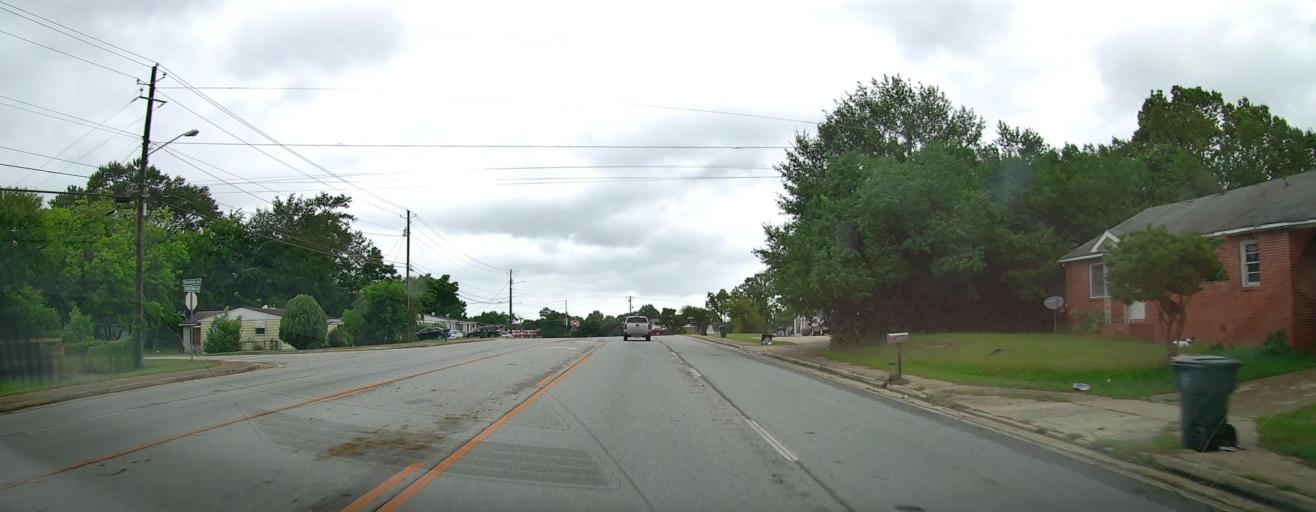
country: US
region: Georgia
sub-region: Bibb County
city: Macon
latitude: 32.8128
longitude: -83.7073
